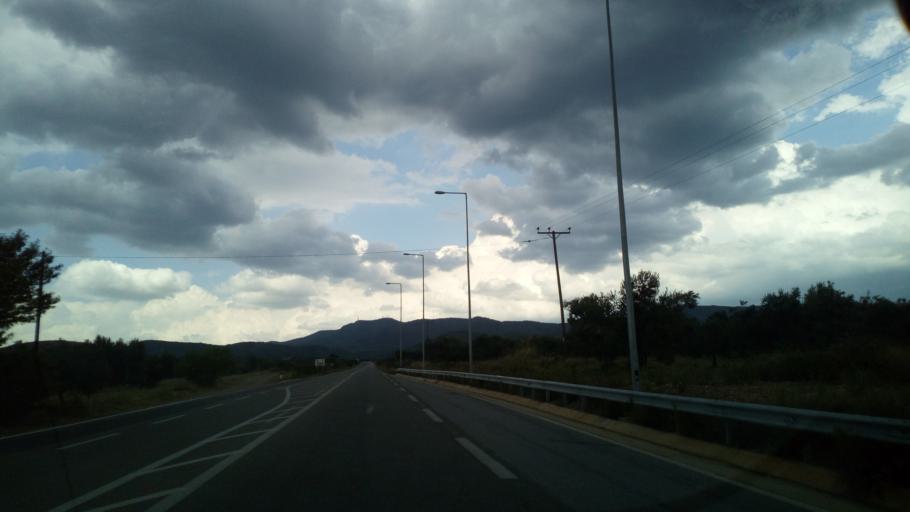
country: GR
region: Central Macedonia
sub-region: Nomos Chalkidikis
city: Polygyros
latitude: 40.3313
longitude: 23.4517
